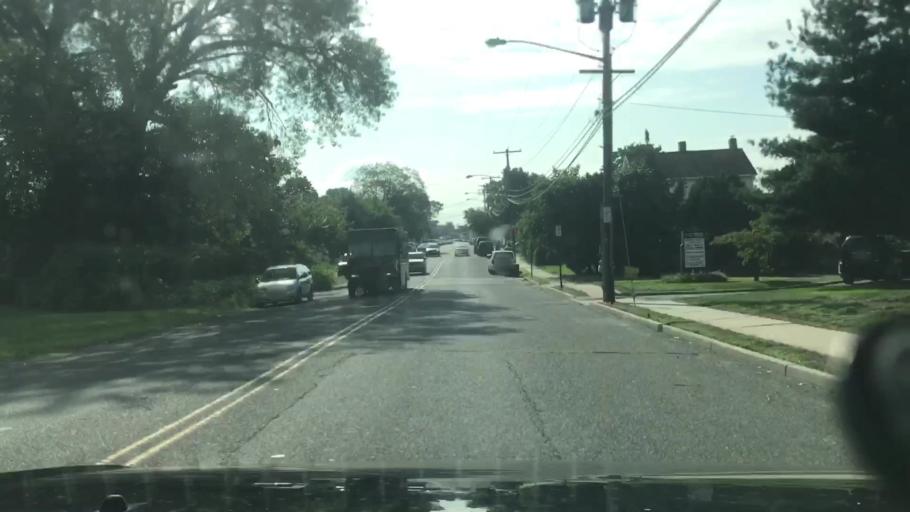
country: US
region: New Jersey
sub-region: Monmouth County
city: Long Branch
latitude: 40.3008
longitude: -73.9965
